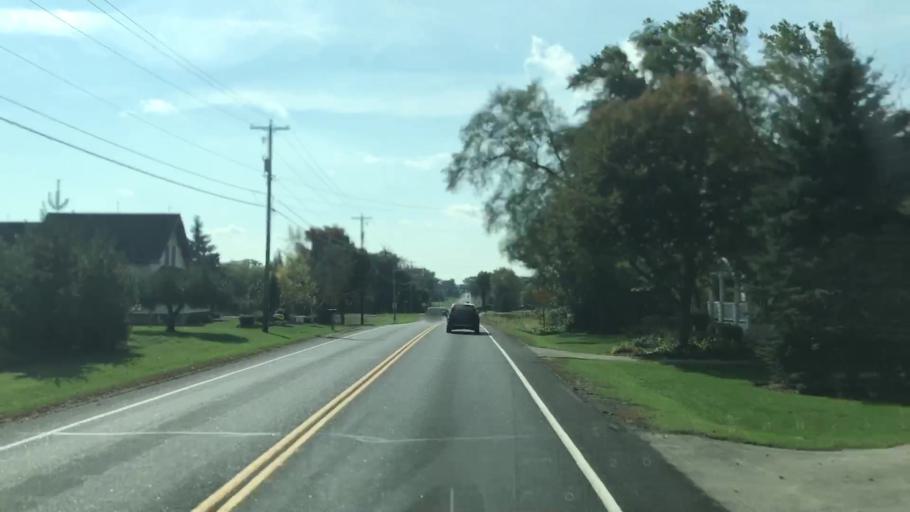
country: US
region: Wisconsin
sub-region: Ozaukee County
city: Mequon
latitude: 43.2086
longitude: -88.0435
